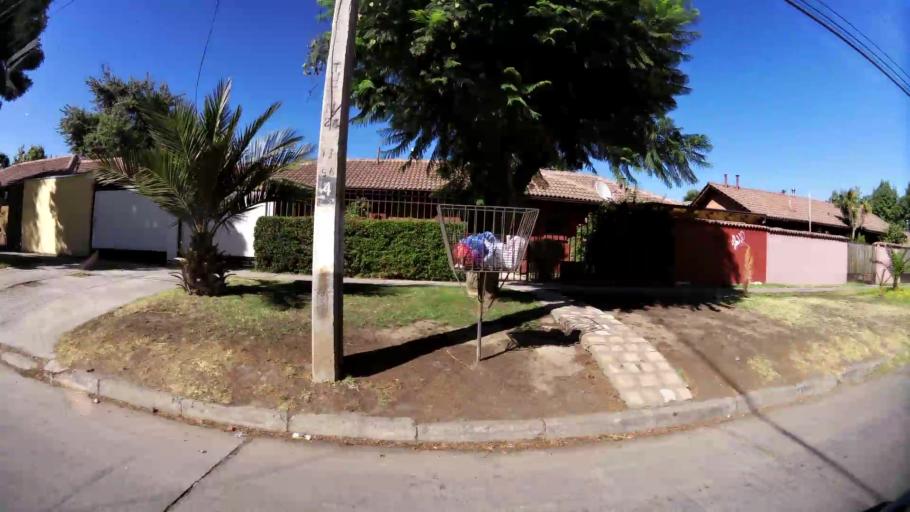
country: CL
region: O'Higgins
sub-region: Provincia de Cachapoal
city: Rancagua
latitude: -34.1819
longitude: -70.7172
